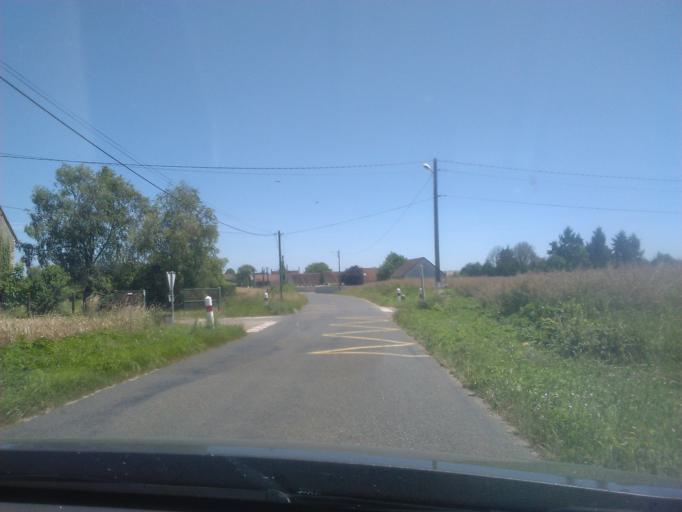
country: FR
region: Centre
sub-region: Departement du Loir-et-Cher
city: Saint-Sulpice-de-Pommeray
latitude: 47.6203
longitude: 1.2128
